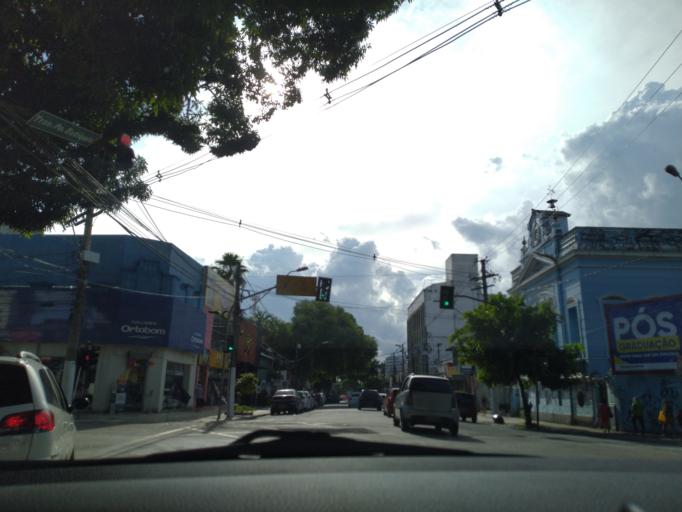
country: BR
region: Para
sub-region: Belem
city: Belem
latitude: -1.4596
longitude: -48.4920
